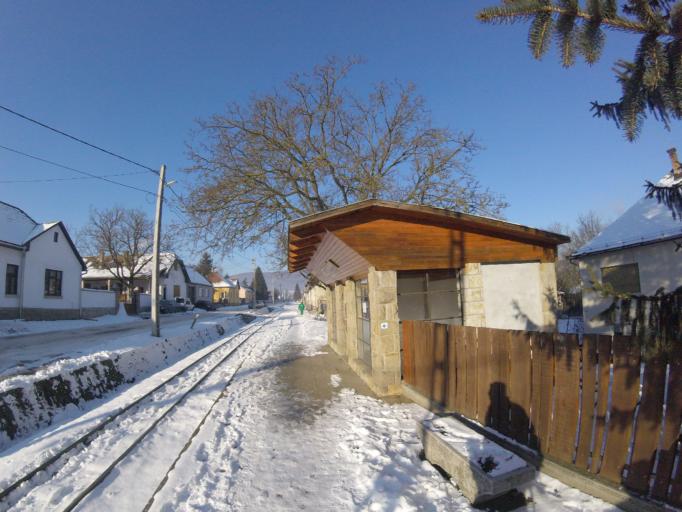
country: HU
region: Pest
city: Kismaros
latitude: 47.8644
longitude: 19.0058
